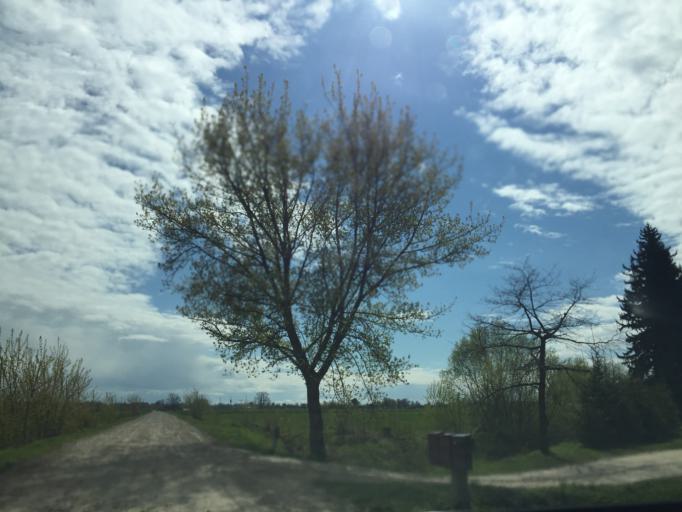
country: LV
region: Jelgava
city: Jelgava
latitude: 56.5735
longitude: 23.7856
